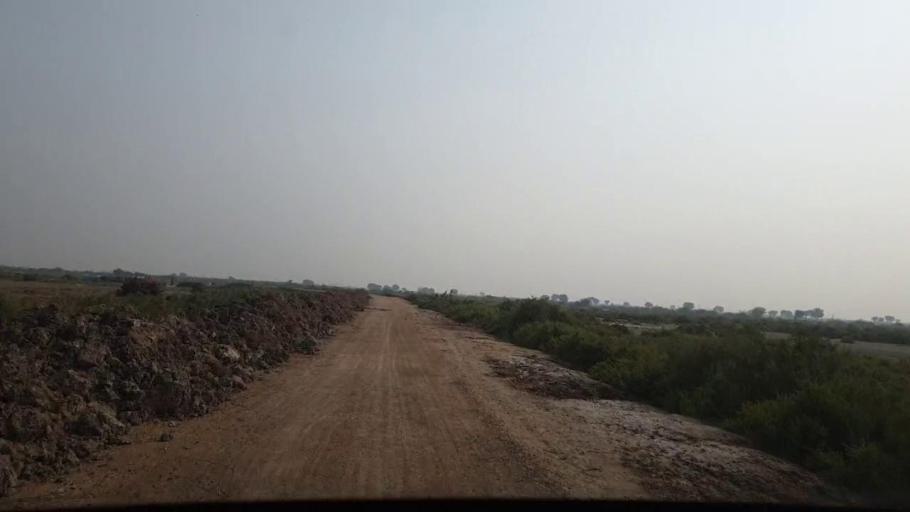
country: PK
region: Sindh
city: Jati
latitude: 24.2823
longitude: 68.4175
